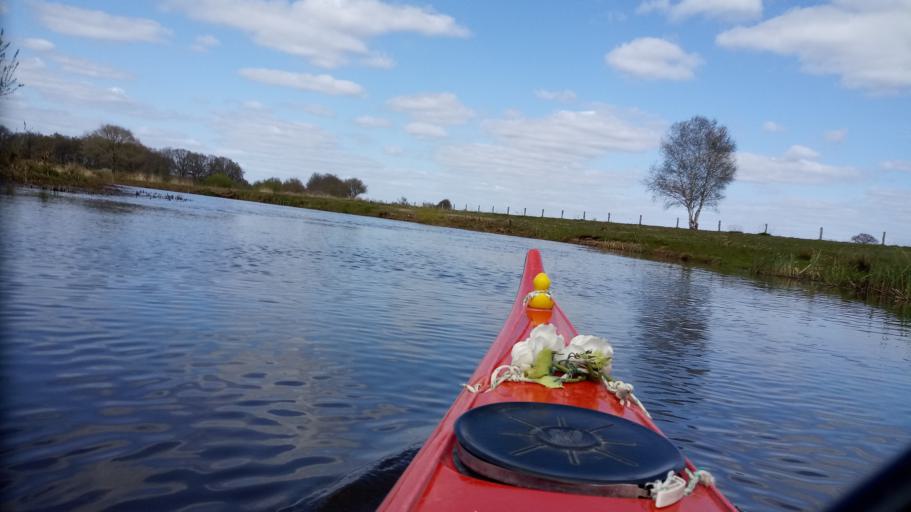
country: NL
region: Overijssel
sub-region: Gemeente Twenterand
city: Den Ham
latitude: 52.4571
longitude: 6.4435
